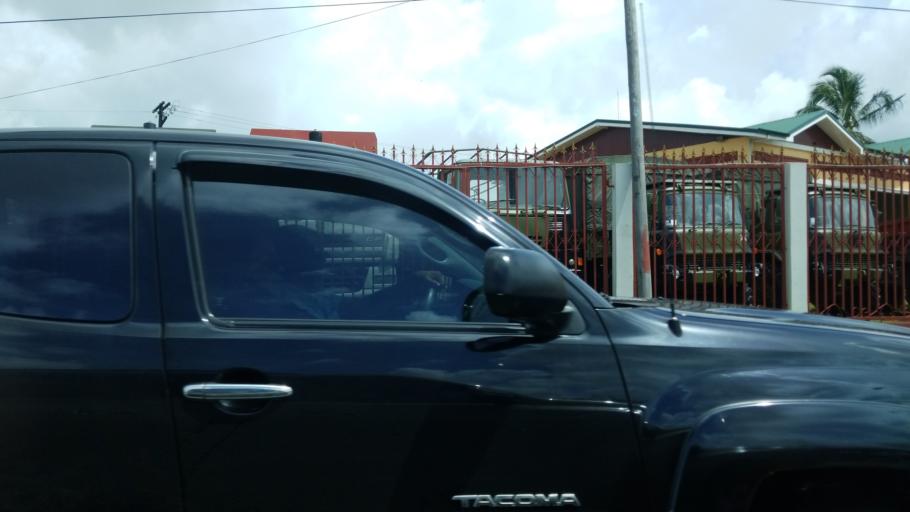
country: GY
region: Demerara-Mahaica
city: Georgetown
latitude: 6.7727
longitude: -58.1736
